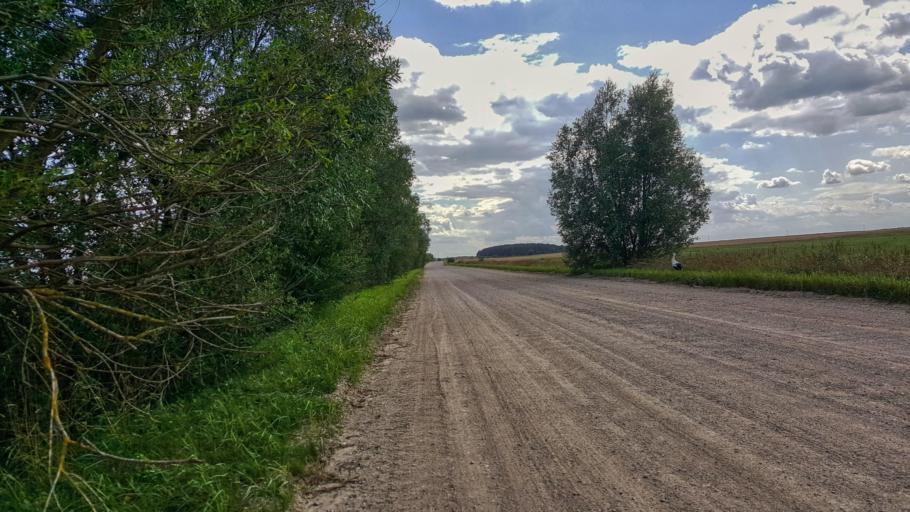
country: BY
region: Brest
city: Kamyanyets
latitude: 52.4161
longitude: 23.8629
